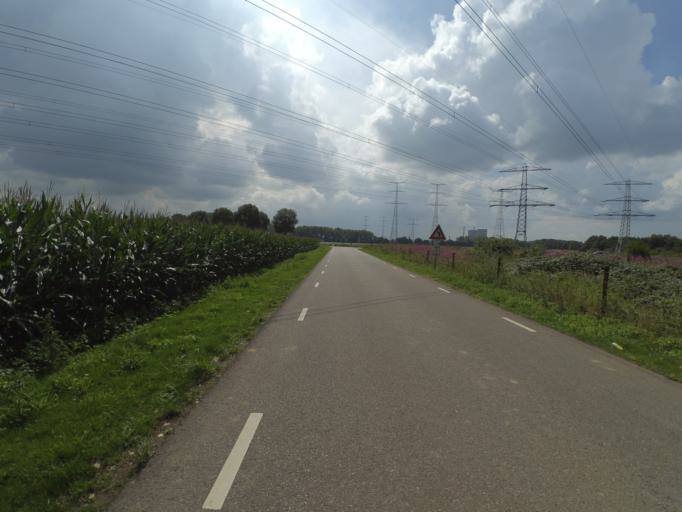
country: NL
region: Limburg
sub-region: Gemeente Maasgouw
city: Maasbracht
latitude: 51.1758
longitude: 5.9121
